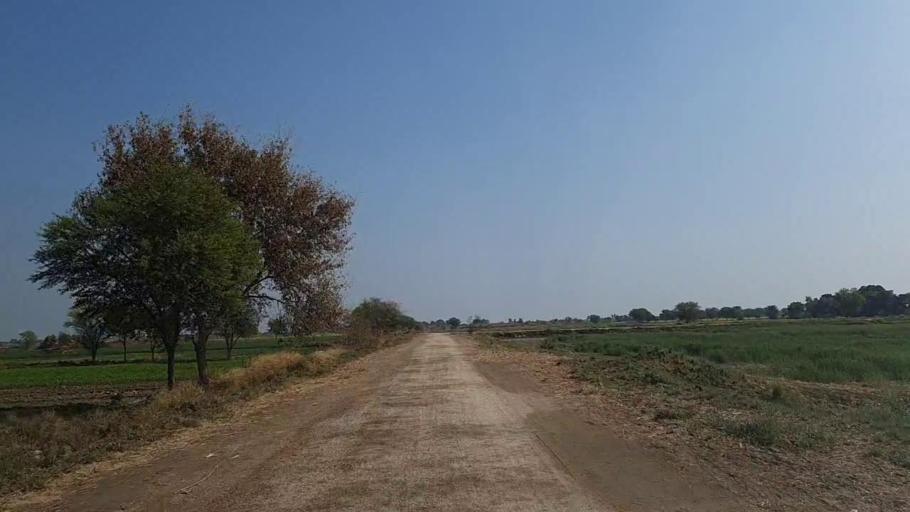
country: PK
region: Sindh
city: Nawabshah
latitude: 26.2532
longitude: 68.4907
